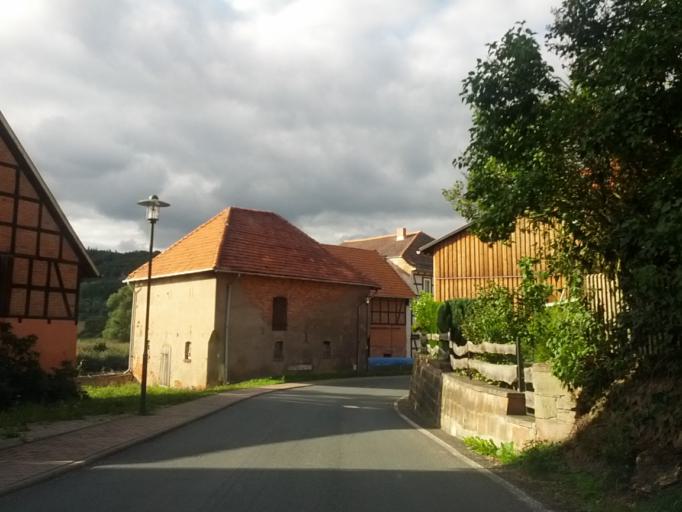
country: DE
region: Thuringia
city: Gerstungen
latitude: 51.0014
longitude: 10.1044
